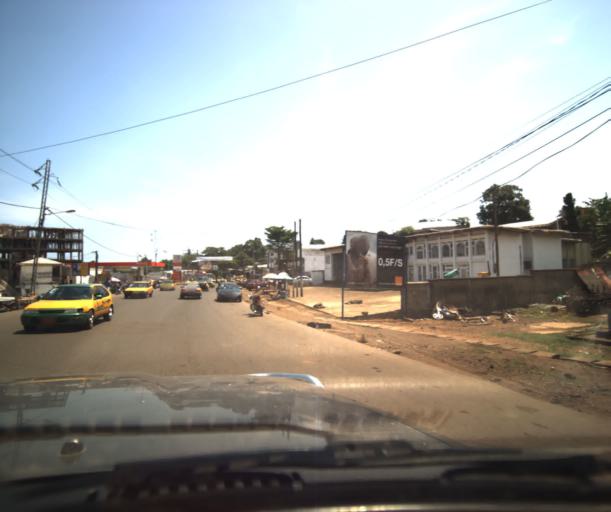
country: CM
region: South-West Province
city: Limbe
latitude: 4.0162
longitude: 9.2083
